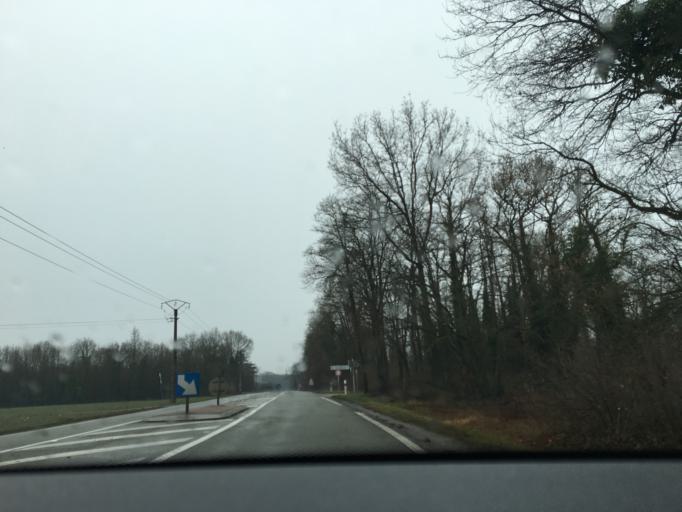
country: FR
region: Ile-de-France
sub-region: Departement des Yvelines
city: Limay
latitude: 49.0202
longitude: 1.7388
